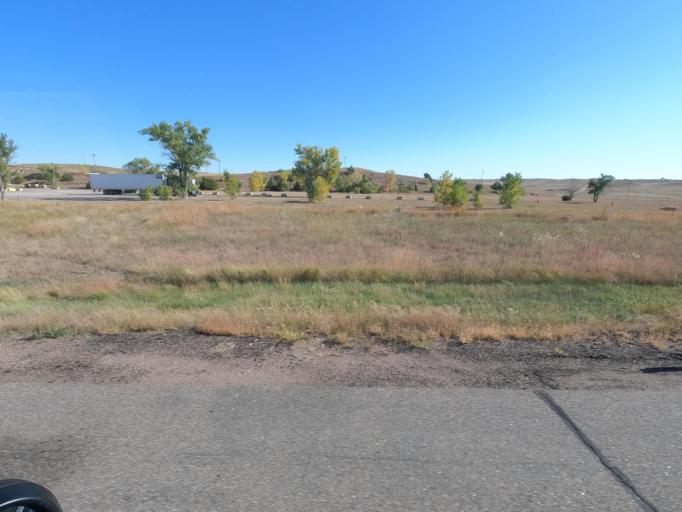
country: US
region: Colorado
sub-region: Sedgwick County
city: Julesburg
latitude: 40.9663
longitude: -102.2486
